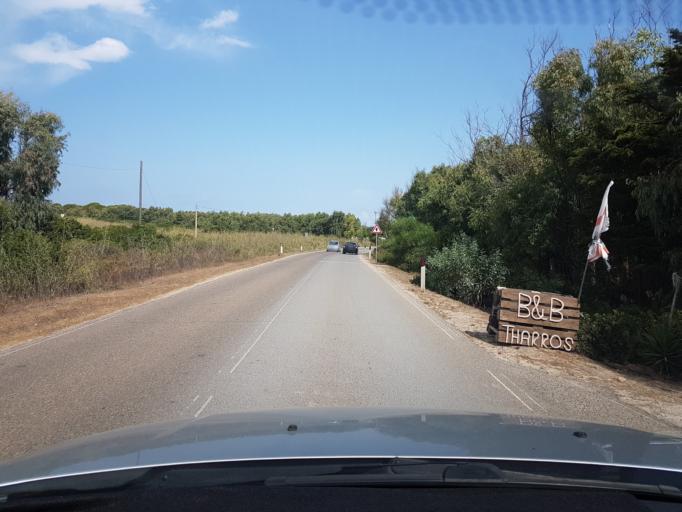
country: IT
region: Sardinia
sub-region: Provincia di Oristano
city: Cabras
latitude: 39.8890
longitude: 8.4355
